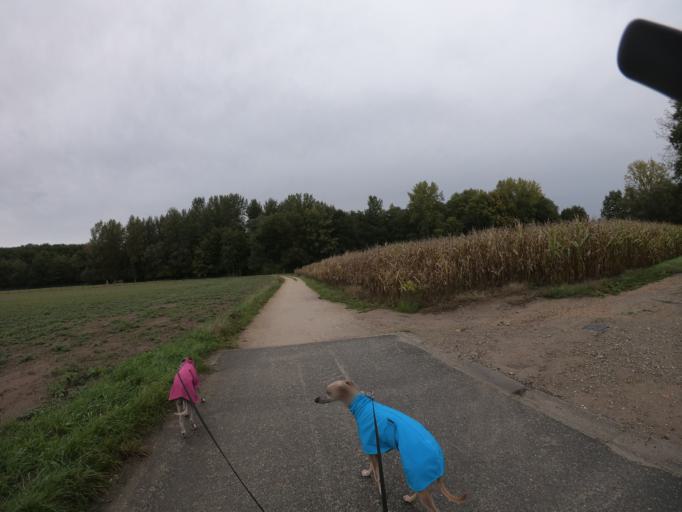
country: BE
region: Flanders
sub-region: Provincie Vlaams-Brabant
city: Rotselaar
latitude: 50.9485
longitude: 4.7334
